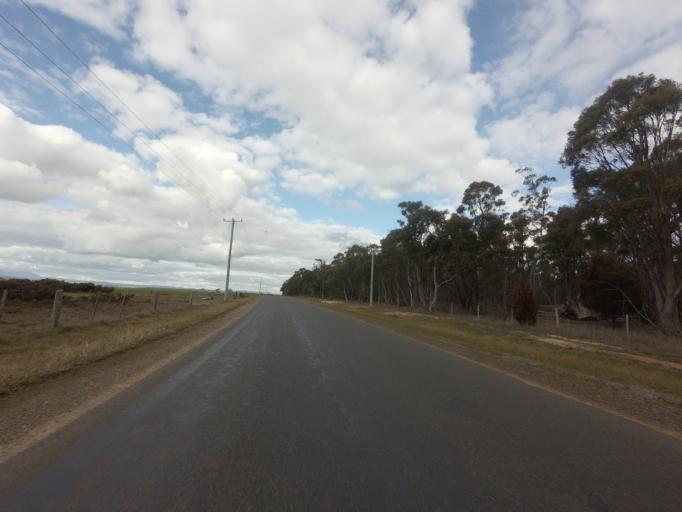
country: AU
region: Tasmania
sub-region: Northern Midlands
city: Longford
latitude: -41.8005
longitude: 147.1325
